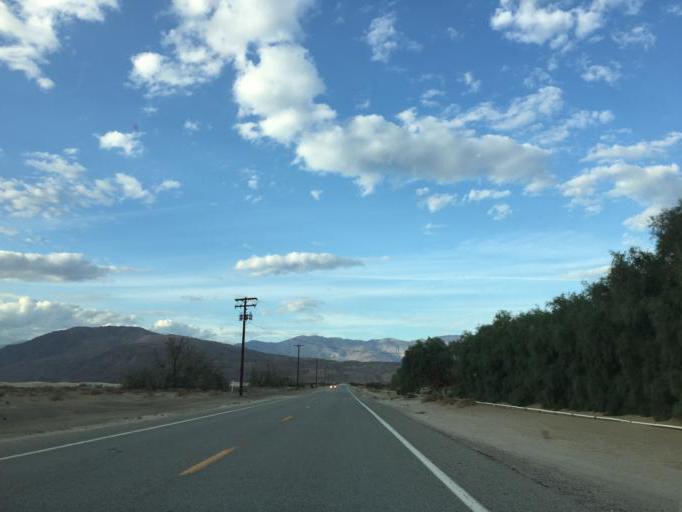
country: US
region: California
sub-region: San Diego County
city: Borrego Springs
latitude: 33.2701
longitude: -116.2988
